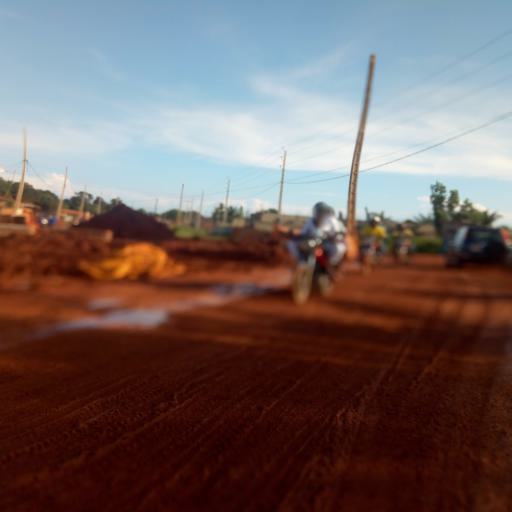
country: BJ
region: Atlantique
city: Hevie
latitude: 6.4194
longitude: 2.2614
